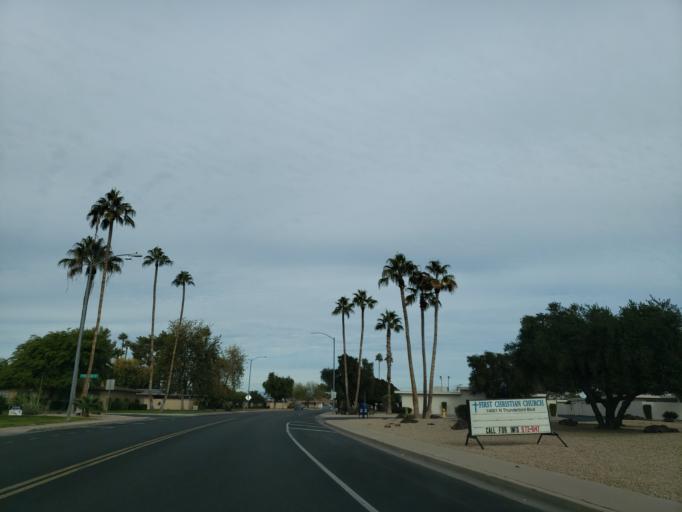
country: US
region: Arizona
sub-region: Maricopa County
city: Youngtown
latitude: 33.6121
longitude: -112.2993
